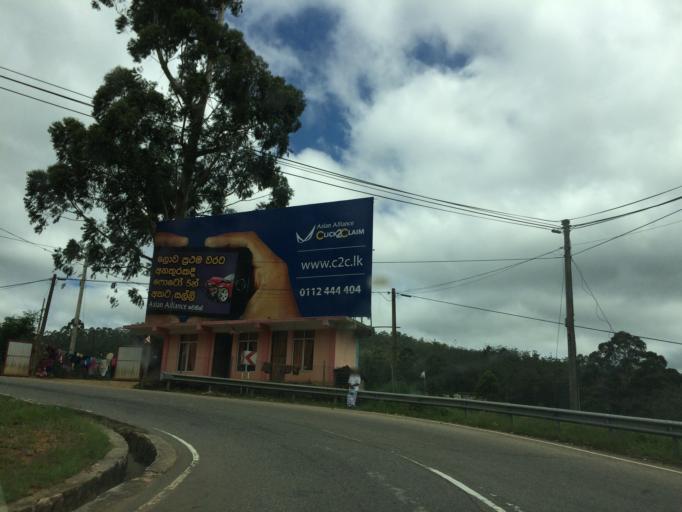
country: LK
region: Central
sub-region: Nuwara Eliya District
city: Nuwara Eliya
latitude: 7.0184
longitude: 80.7271
